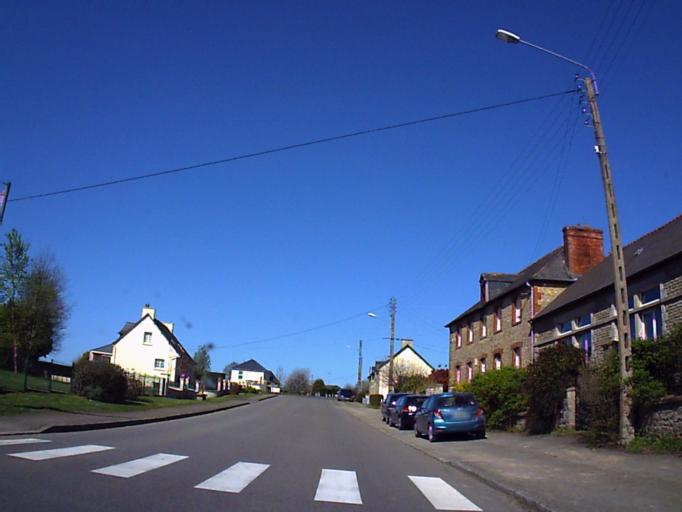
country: FR
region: Brittany
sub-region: Departement des Cotes-d'Armor
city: Caulnes
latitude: 48.2675
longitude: -2.1631
